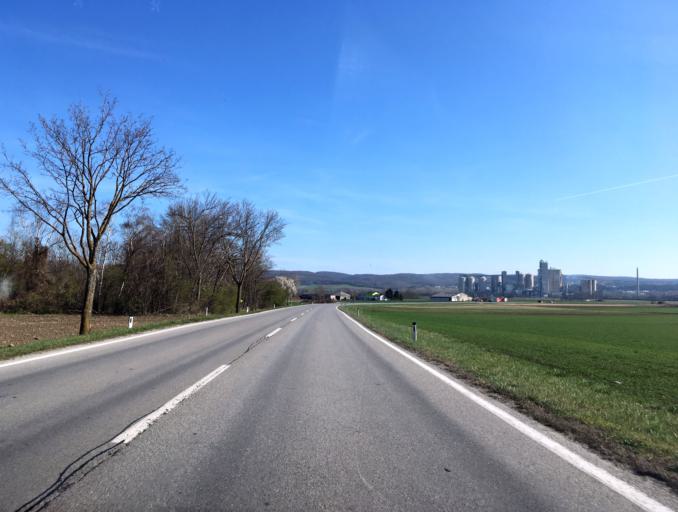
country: AT
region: Lower Austria
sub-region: Politischer Bezirk Bruck an der Leitha
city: Gotzendorf an der Leitha
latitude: 48.0007
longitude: 16.5969
